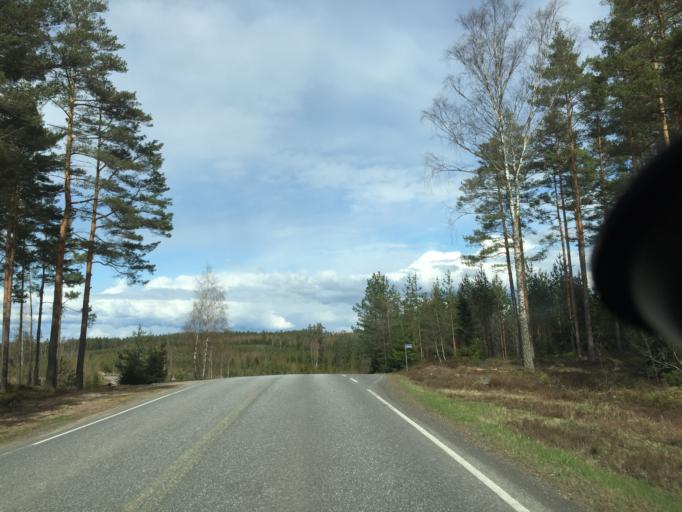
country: FI
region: Varsinais-Suomi
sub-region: Salo
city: Pernioe
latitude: 60.0320
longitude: 23.1847
